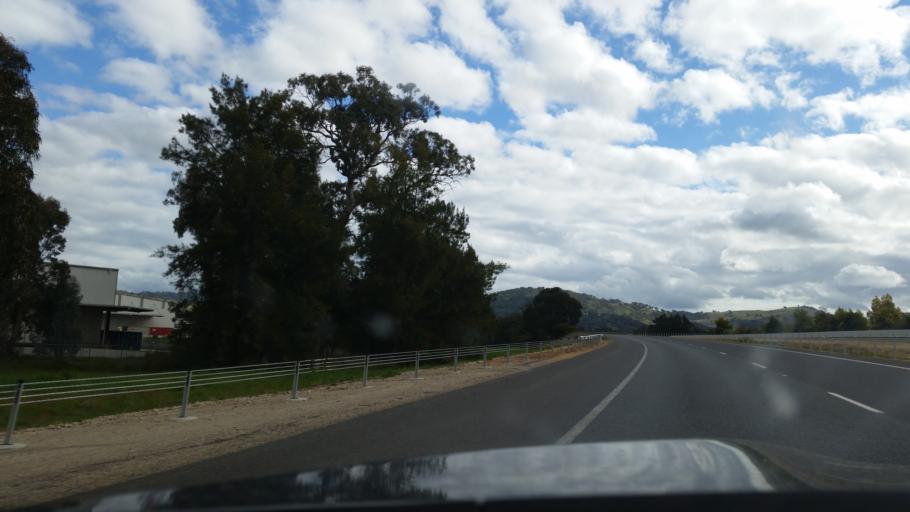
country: AU
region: Victoria
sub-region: Wodonga
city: Wodonga
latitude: -36.1072
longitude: 146.8655
